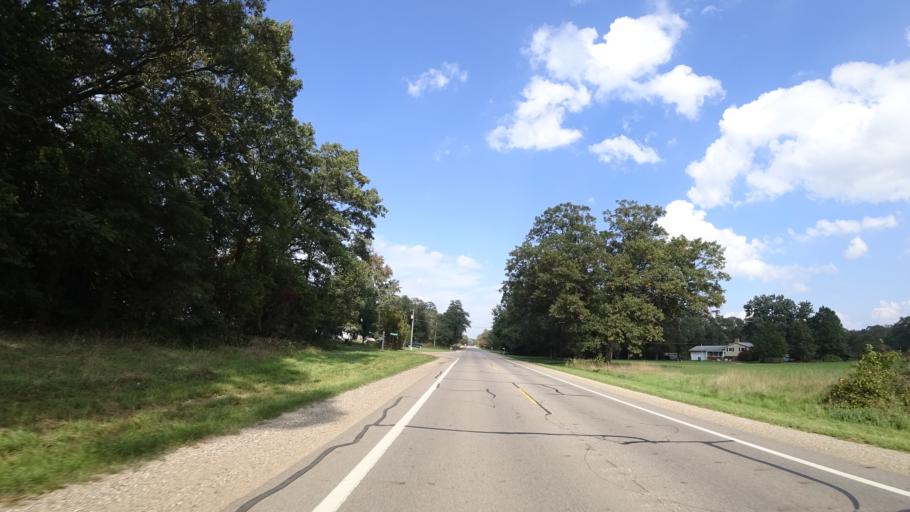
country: US
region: Michigan
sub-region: Saint Joseph County
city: Centreville
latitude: 41.9930
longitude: -85.5617
